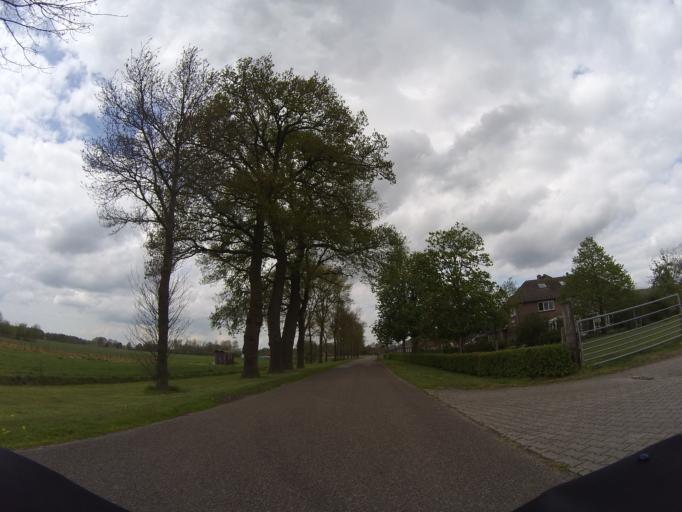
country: NL
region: Overijssel
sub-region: Gemeente Twenterand
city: Magele
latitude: 52.5263
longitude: 6.5093
